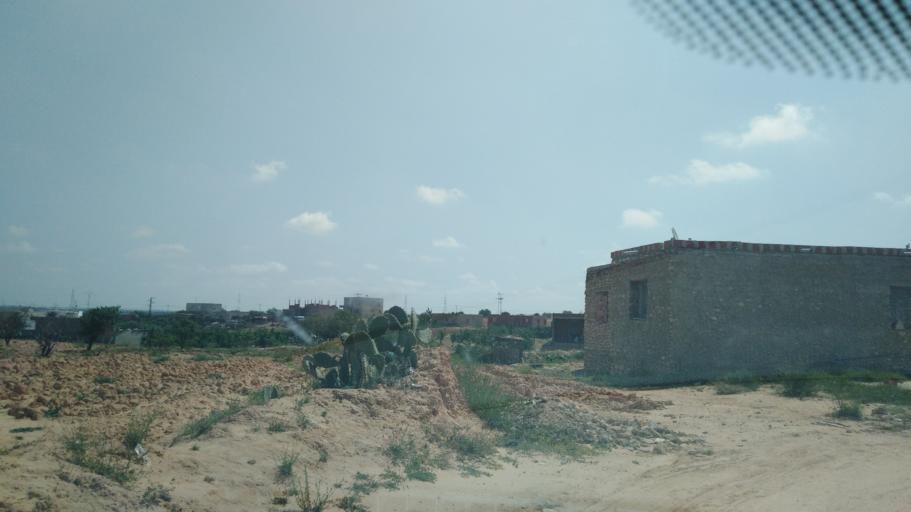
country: TN
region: Safaqis
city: Sfax
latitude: 34.7274
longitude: 10.5732
